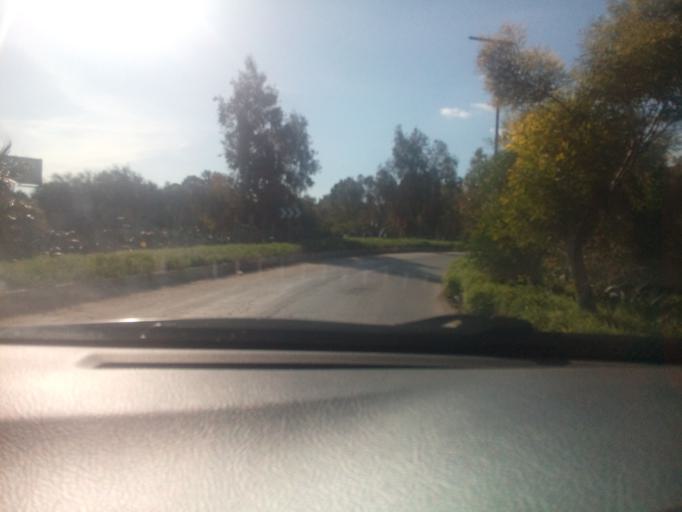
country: DZ
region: Oran
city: Es Senia
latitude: 35.6666
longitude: -0.5945
